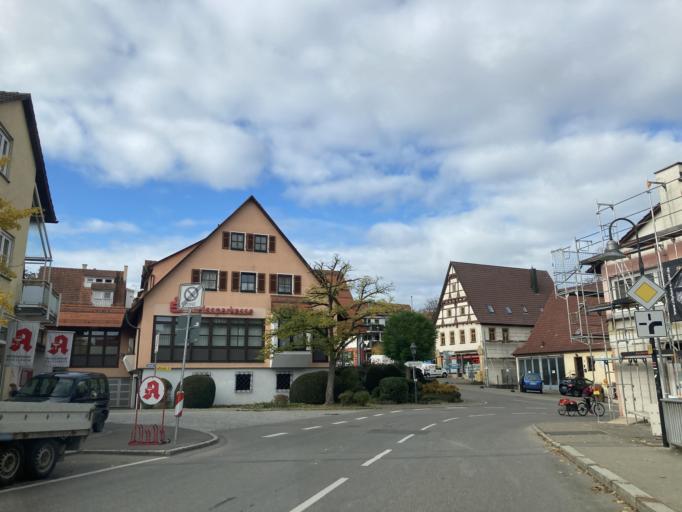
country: DE
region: Baden-Wuerttemberg
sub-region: Tuebingen Region
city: Dusslingen
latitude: 48.4501
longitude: 9.0558
